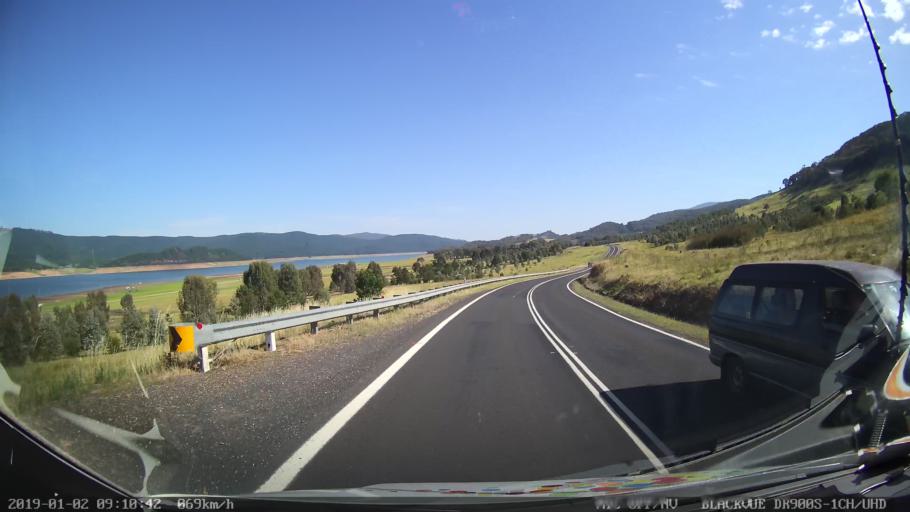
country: AU
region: New South Wales
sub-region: Tumut Shire
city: Tumut
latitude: -35.5192
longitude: 148.2683
